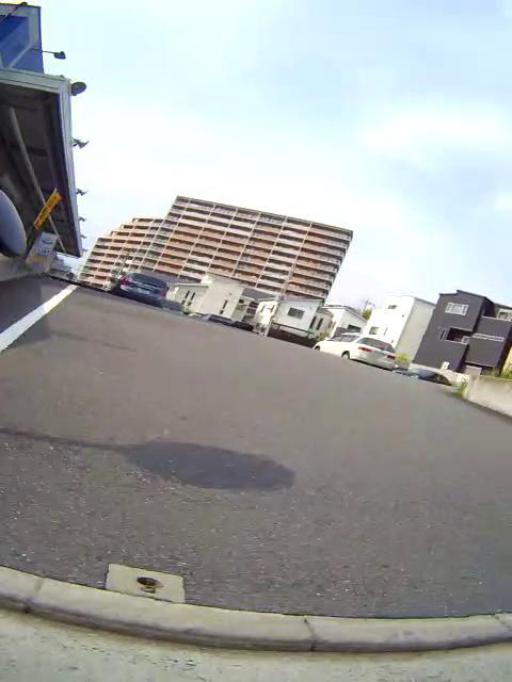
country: JP
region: Osaka
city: Toyonaka
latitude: 34.7807
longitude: 135.4898
